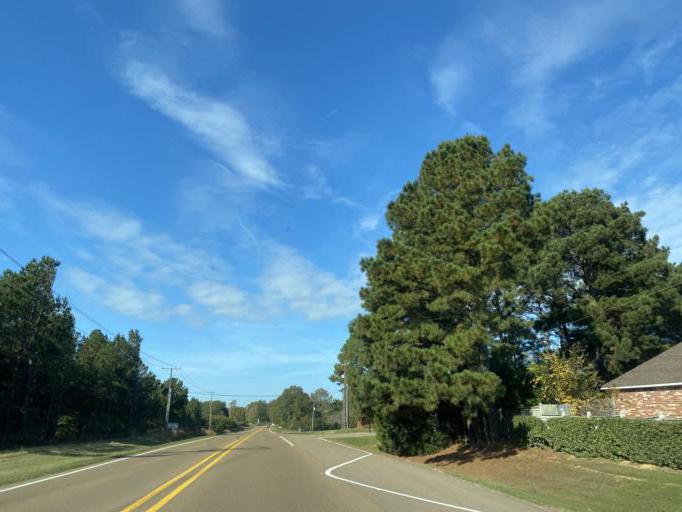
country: US
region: Mississippi
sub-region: Madison County
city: Madison
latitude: 32.4815
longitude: -90.1697
